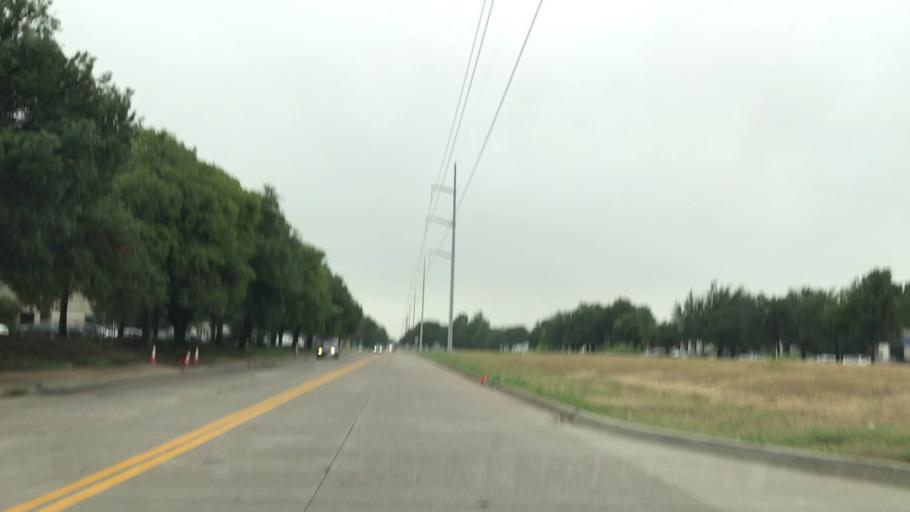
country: US
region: Texas
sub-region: Dallas County
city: Coppell
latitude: 32.9350
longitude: -97.0199
